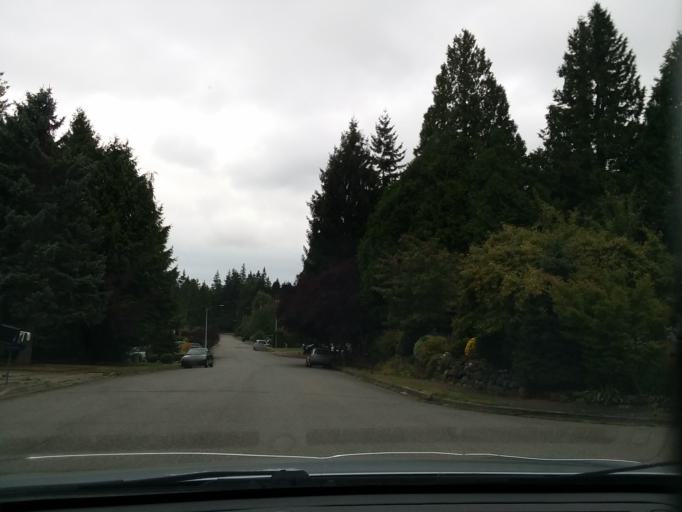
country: US
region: Washington
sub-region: Snohomish County
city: Alderwood Manor
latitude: 47.8257
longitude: -122.2880
